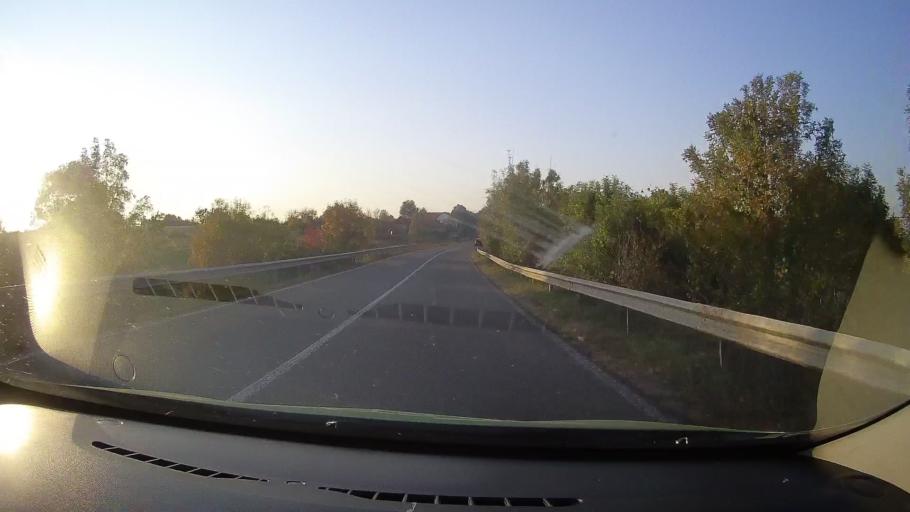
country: RO
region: Arad
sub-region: Comuna Barsa
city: Barsa
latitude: 46.3957
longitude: 22.0361
